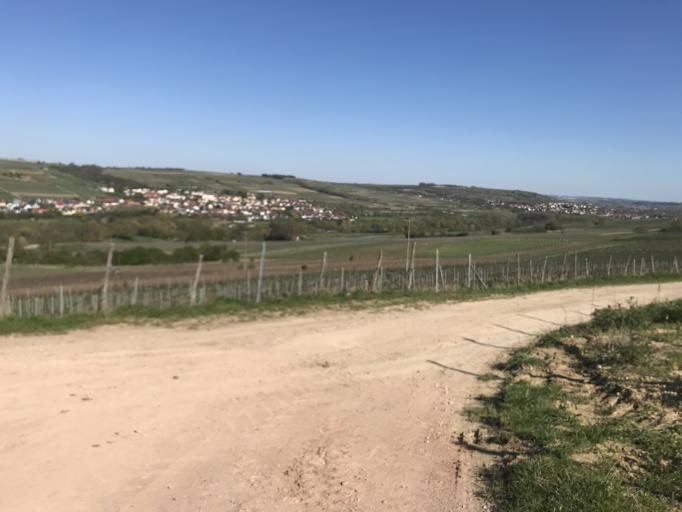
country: DE
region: Rheinland-Pfalz
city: Bubenheim
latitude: 49.9413
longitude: 8.0605
